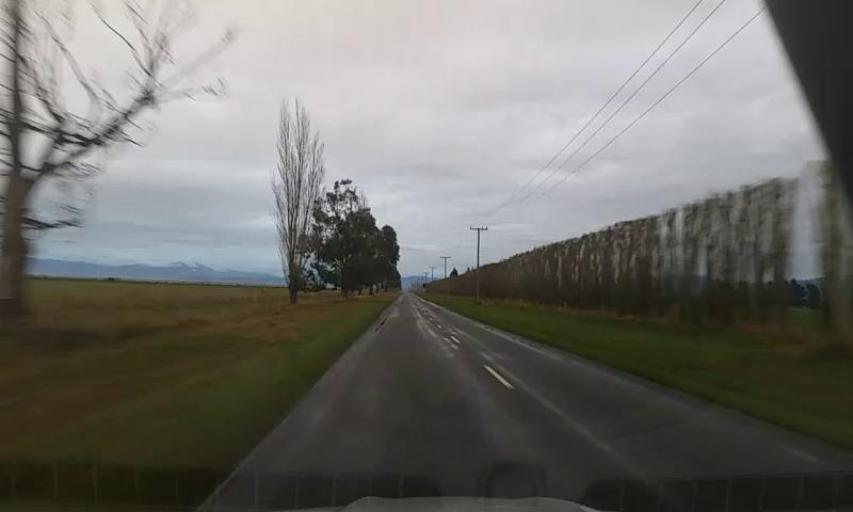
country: NZ
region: Canterbury
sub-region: Ashburton District
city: Methven
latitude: -43.7394
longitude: 171.6801
